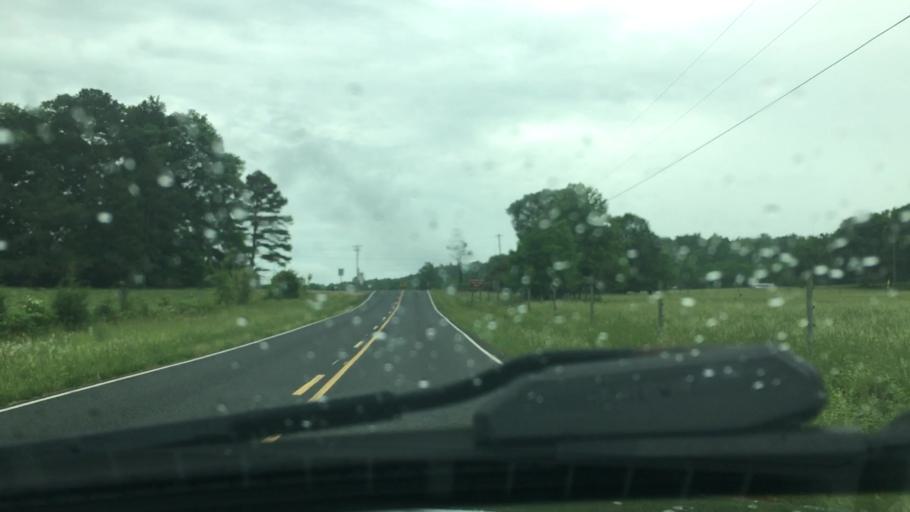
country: US
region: North Carolina
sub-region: Stanly County
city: Badin
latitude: 35.3747
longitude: -80.1167
